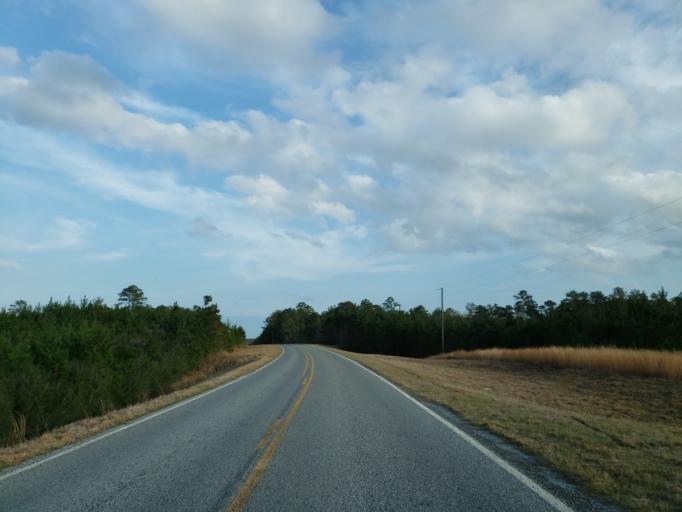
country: US
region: Mississippi
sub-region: Clarke County
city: Stonewall
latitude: 32.1758
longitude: -88.7027
